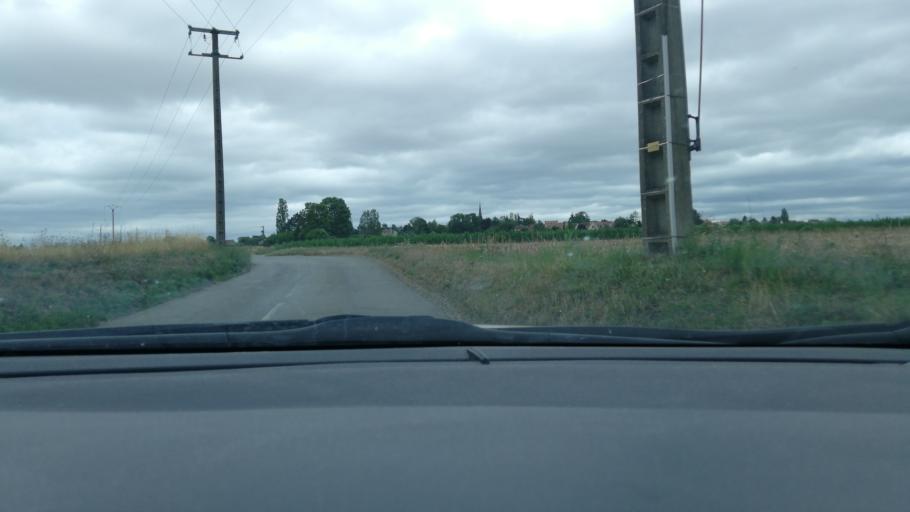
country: FR
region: Ile-de-France
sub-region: Departement du Val-d'Oise
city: Ennery
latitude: 49.0935
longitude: 2.0867
